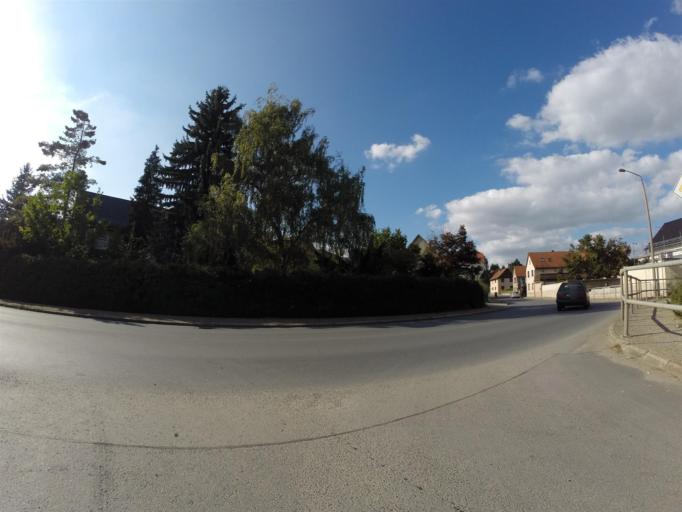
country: DE
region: Thuringia
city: Rothenstein
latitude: 50.8494
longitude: 11.6067
